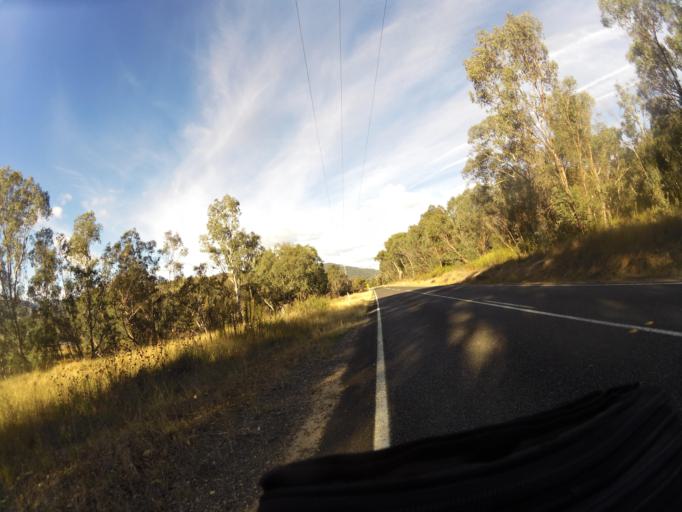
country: AU
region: New South Wales
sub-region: Greater Hume Shire
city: Holbrook
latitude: -35.9917
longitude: 147.8517
